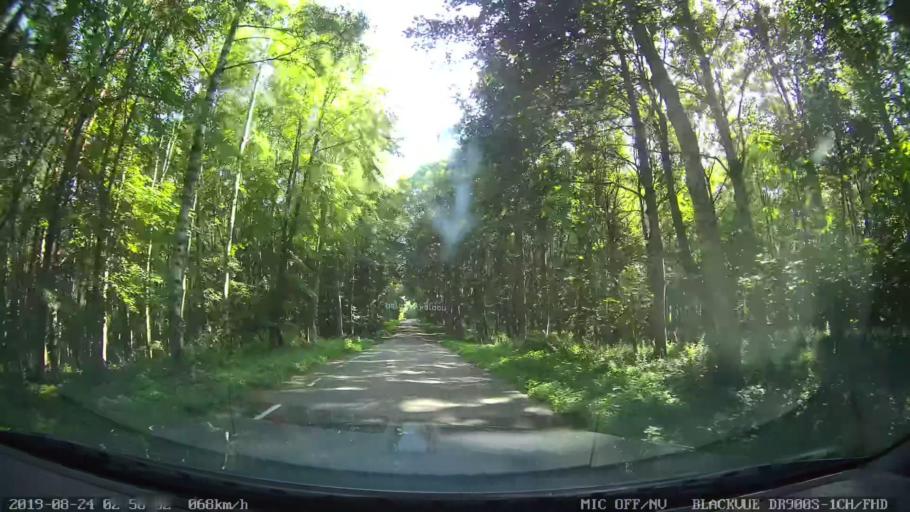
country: SE
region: Skane
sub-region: Skurups Kommun
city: Skurup
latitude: 55.4784
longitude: 13.4126
